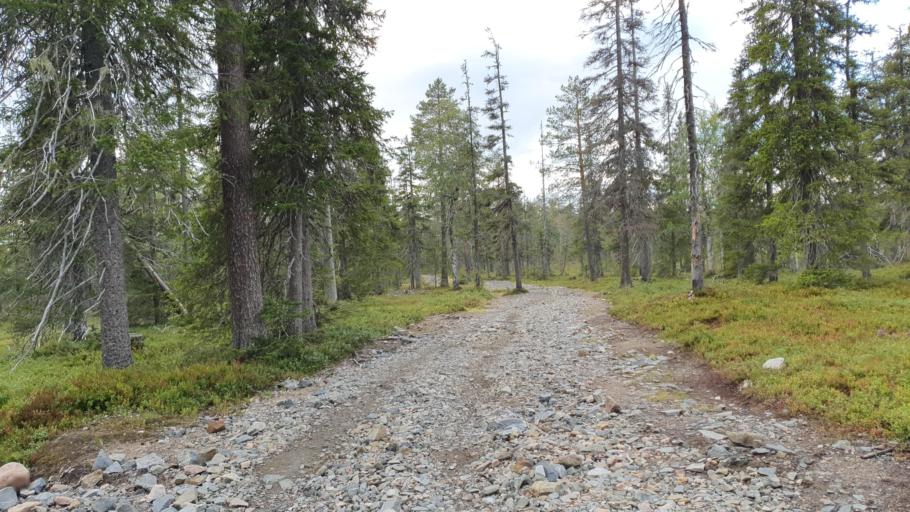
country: FI
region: Lapland
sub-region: Tunturi-Lappi
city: Kolari
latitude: 67.6184
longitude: 24.2323
